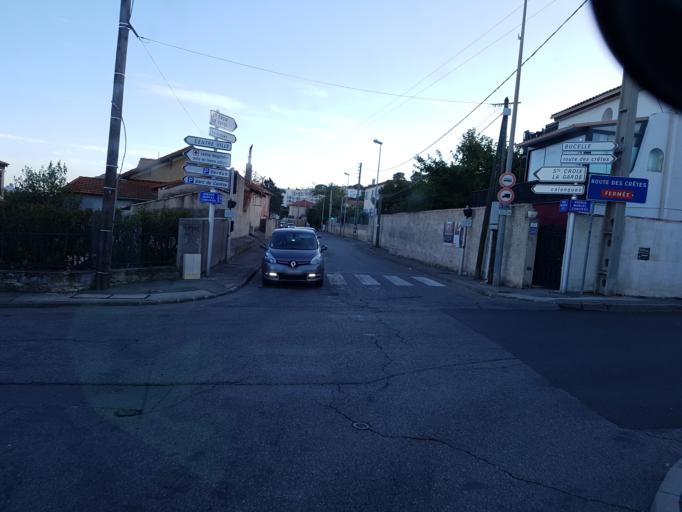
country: FR
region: Provence-Alpes-Cote d'Azur
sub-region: Departement des Bouches-du-Rhone
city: La Ciotat
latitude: 43.1789
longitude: 5.5975
